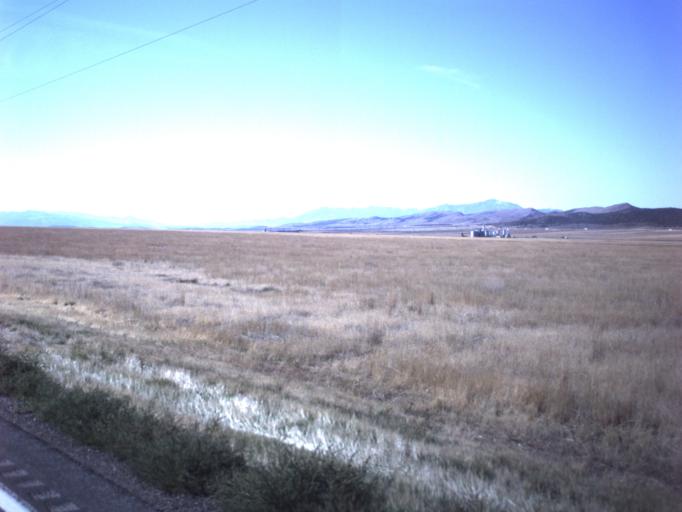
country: US
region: Utah
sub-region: Juab County
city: Nephi
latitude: 39.6342
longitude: -111.8616
